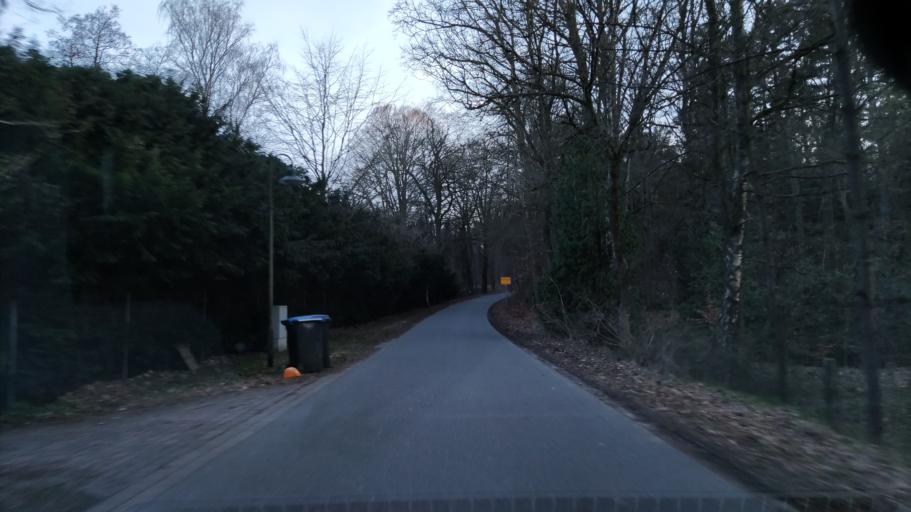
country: DE
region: Lower Saxony
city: Thomasburg
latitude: 53.2035
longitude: 10.6783
